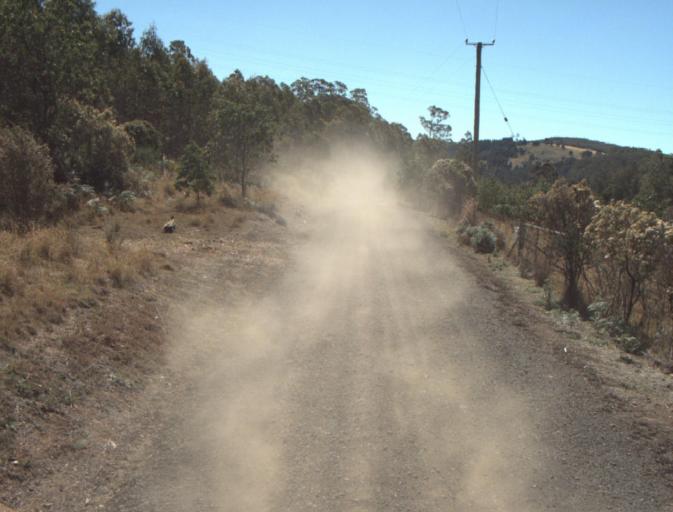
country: AU
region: Tasmania
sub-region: Dorset
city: Scottsdale
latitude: -41.3180
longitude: 147.3835
